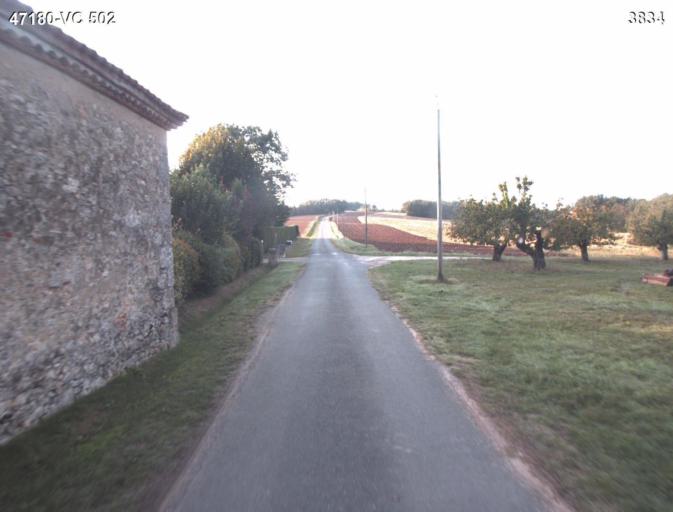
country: FR
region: Aquitaine
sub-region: Departement du Lot-et-Garonne
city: Sainte-Colombe-en-Bruilhois
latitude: 44.1909
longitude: 0.4812
